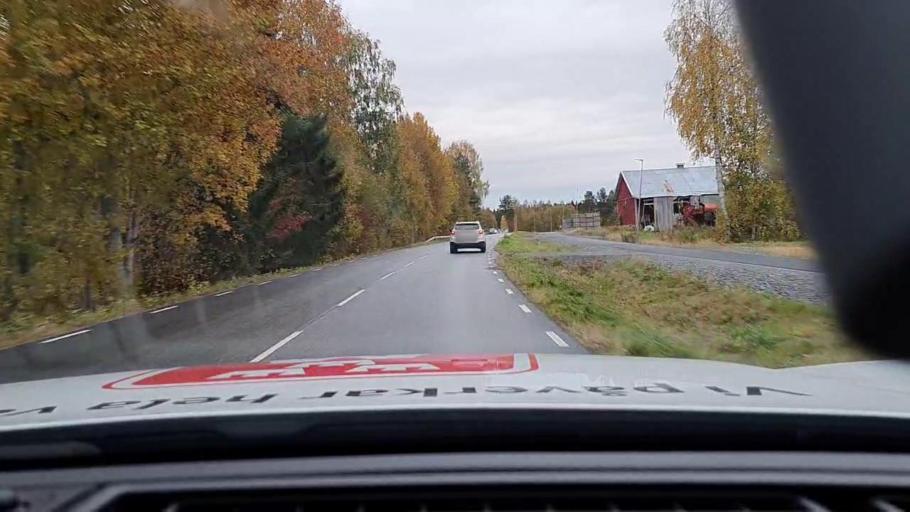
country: SE
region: Norrbotten
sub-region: Bodens Kommun
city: Saevast
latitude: 65.7702
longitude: 21.7048
